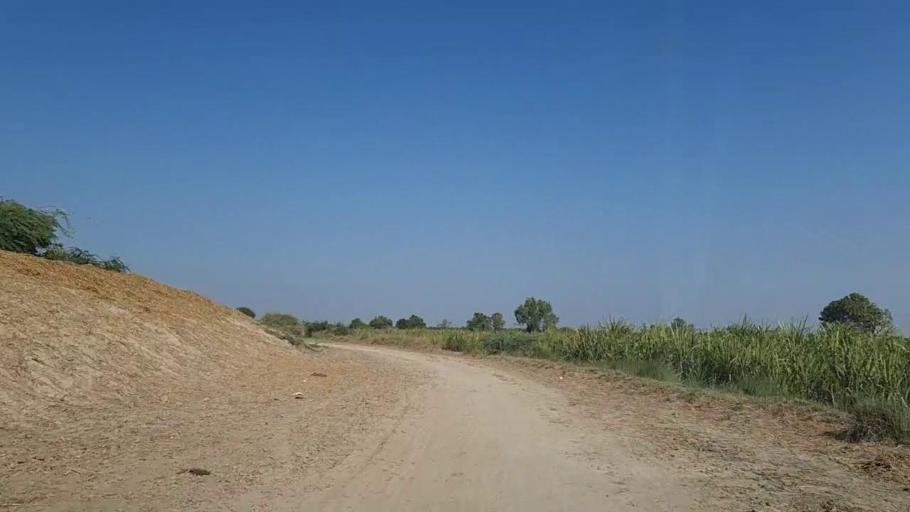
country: PK
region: Sindh
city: Thatta
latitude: 24.5853
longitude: 68.0371
